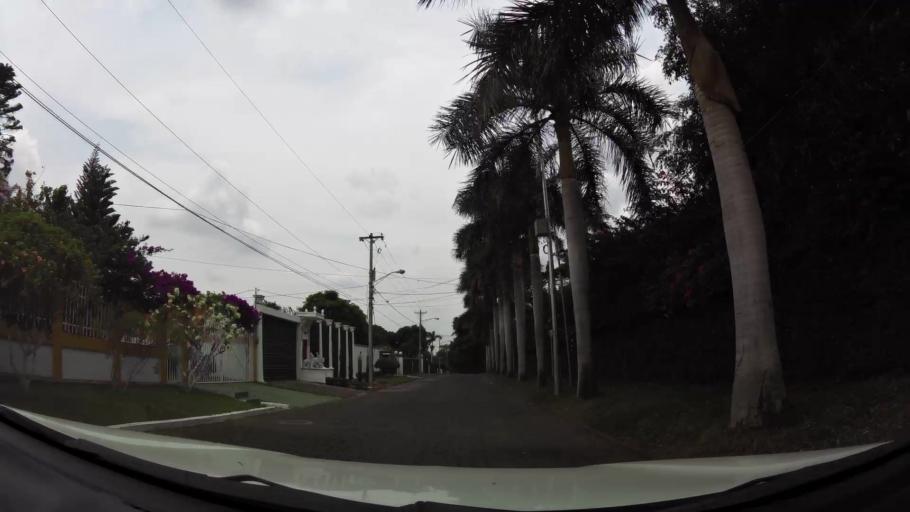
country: NI
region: Managua
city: Managua
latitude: 12.0903
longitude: -86.2312
